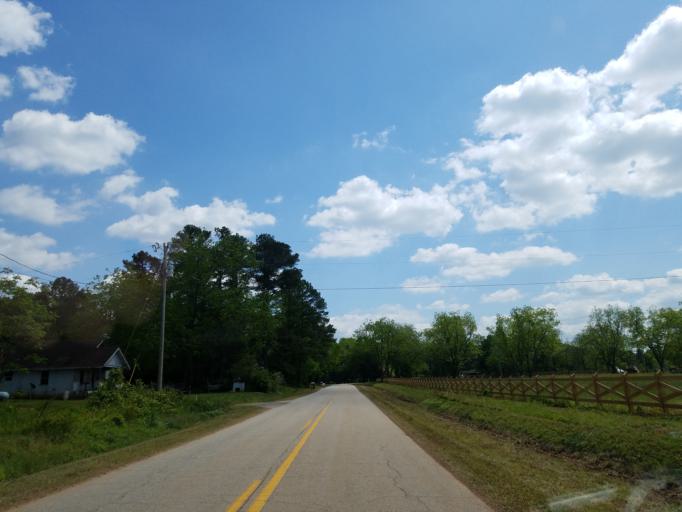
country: US
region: Georgia
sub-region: Monroe County
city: Forsyth
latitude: 33.0950
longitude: -83.9633
